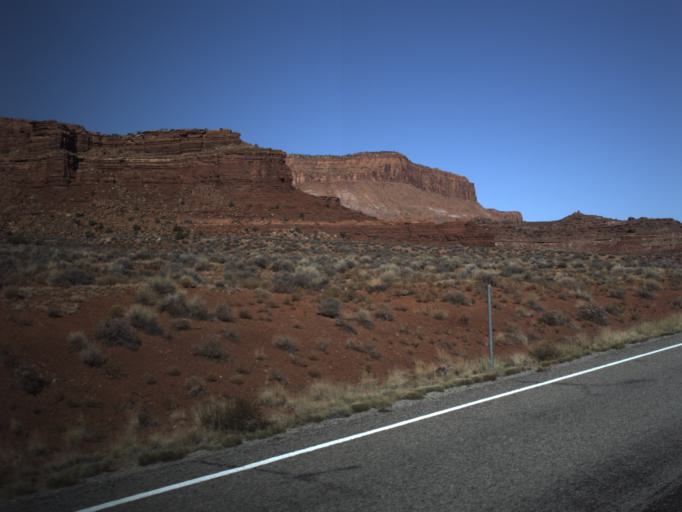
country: US
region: Utah
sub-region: San Juan County
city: Blanding
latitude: 37.7557
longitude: -110.2814
